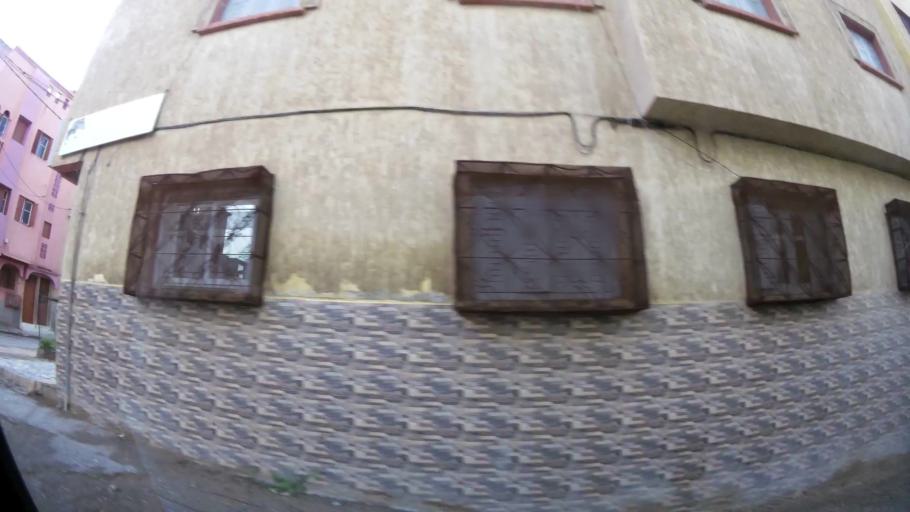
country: MA
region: Chaouia-Ouardigha
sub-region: Settat Province
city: Settat
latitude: 33.0081
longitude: -7.6278
